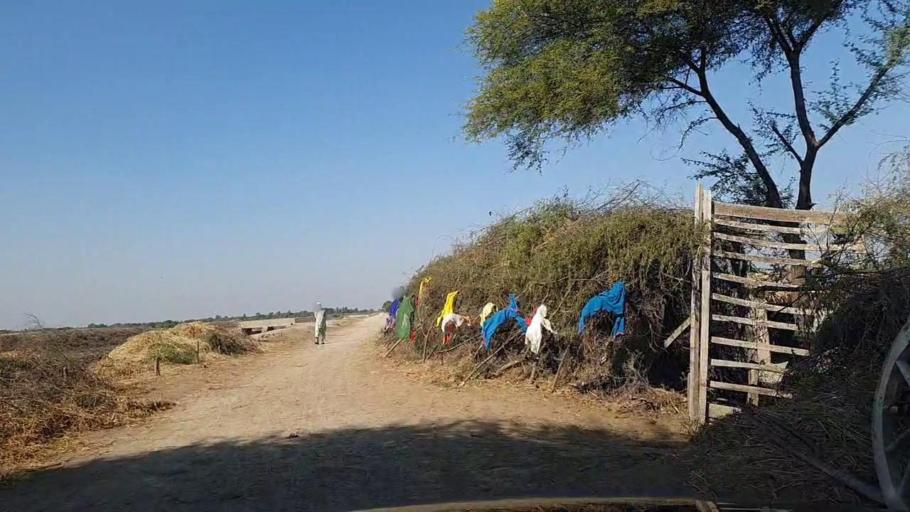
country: PK
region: Sindh
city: Mirpur Batoro
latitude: 24.7218
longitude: 68.2338
